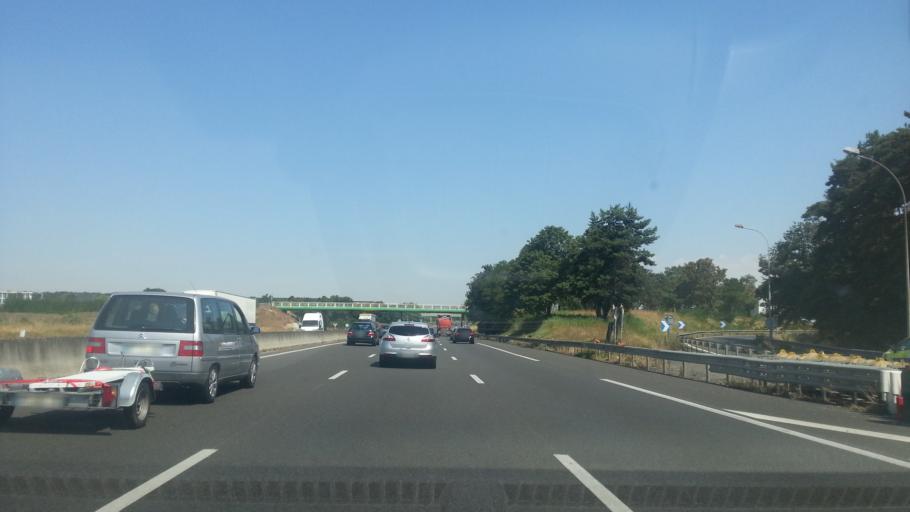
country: FR
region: Centre
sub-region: Departement du Loiret
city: Saran
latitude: 47.9486
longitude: 1.8489
